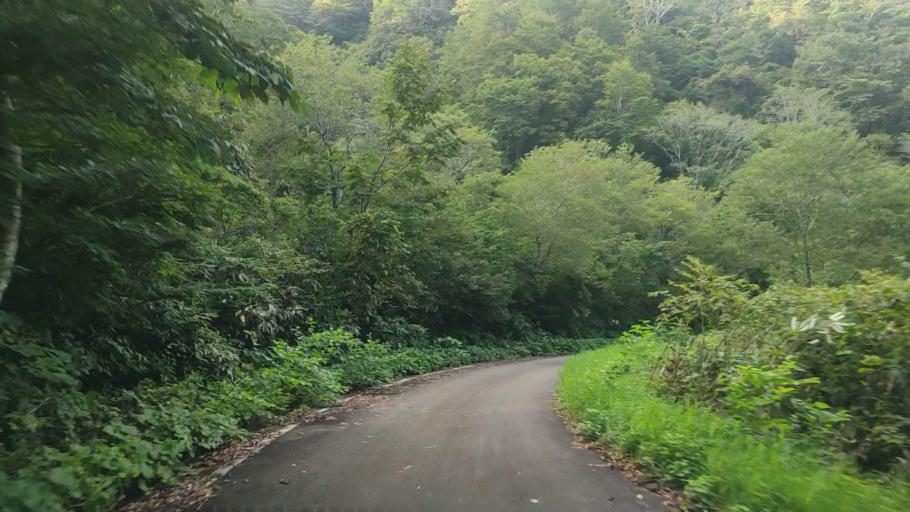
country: JP
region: Toyama
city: Yatsuomachi-higashikumisaka
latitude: 36.3760
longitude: 137.0799
